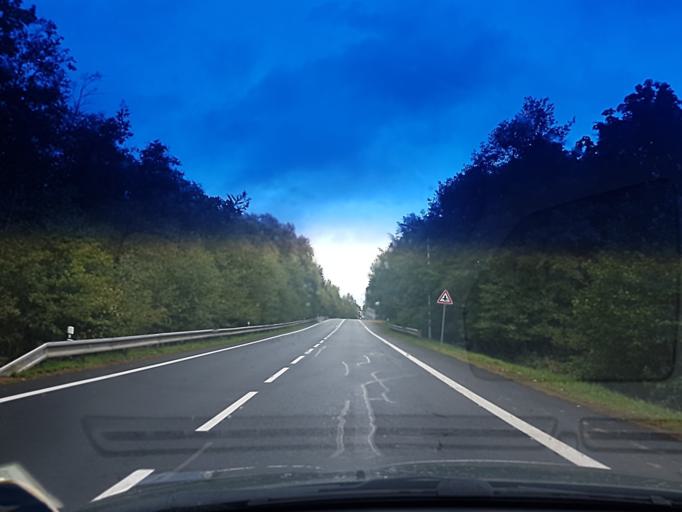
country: CZ
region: Karlovarsky
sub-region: Okres Cheb
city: Frantiskovy Lazne
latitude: 50.0850
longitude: 12.2969
